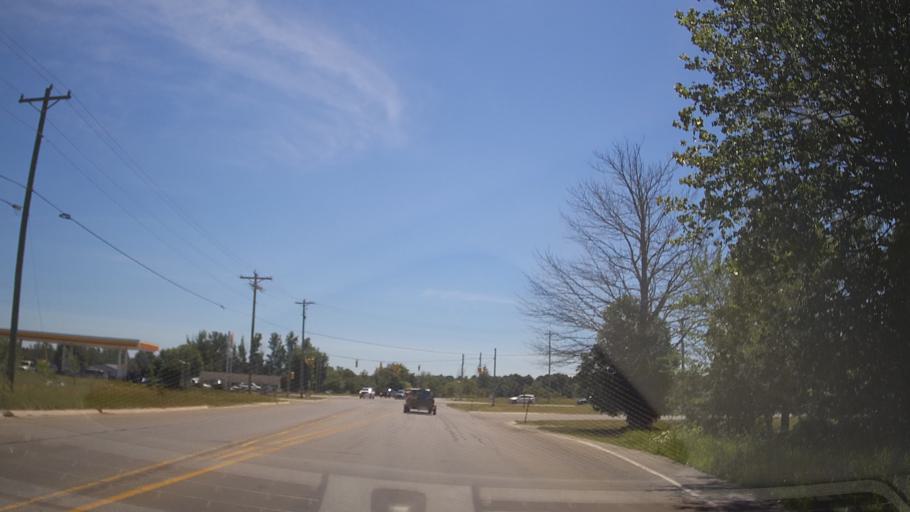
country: US
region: Michigan
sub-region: Grand Traverse County
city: Traverse City
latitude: 44.6662
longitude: -85.6902
